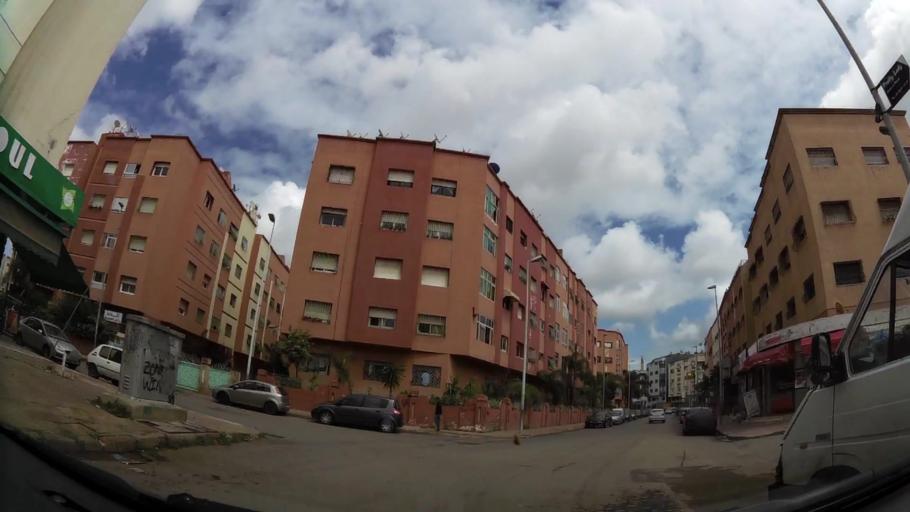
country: MA
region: Grand Casablanca
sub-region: Casablanca
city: Casablanca
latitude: 33.5349
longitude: -7.6071
